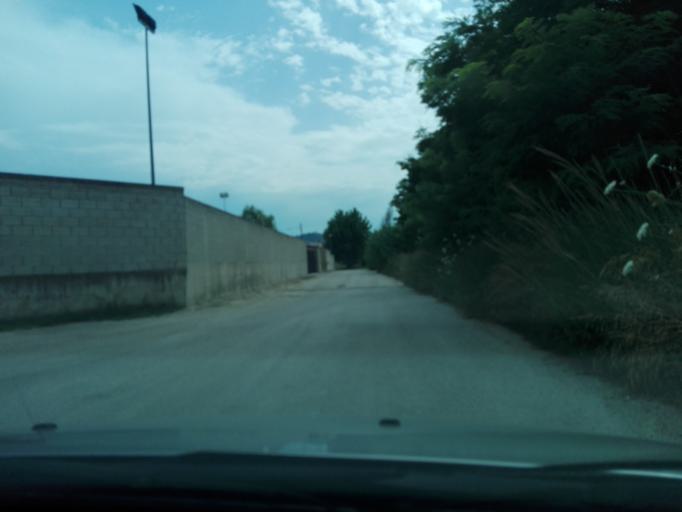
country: IT
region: Abruzzo
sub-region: Provincia di Pescara
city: Cappelle sul Tavo
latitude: 42.4874
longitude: 14.1115
